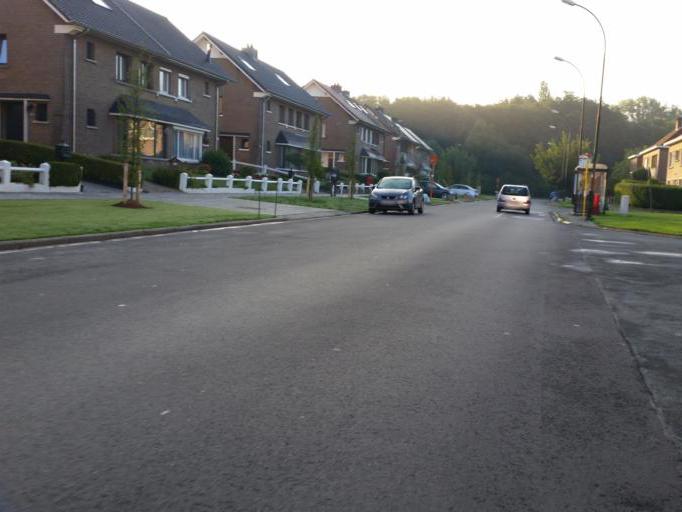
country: BE
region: Flanders
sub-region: Provincie Vlaams-Brabant
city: Vilvoorde
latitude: 50.9199
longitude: 4.4060
